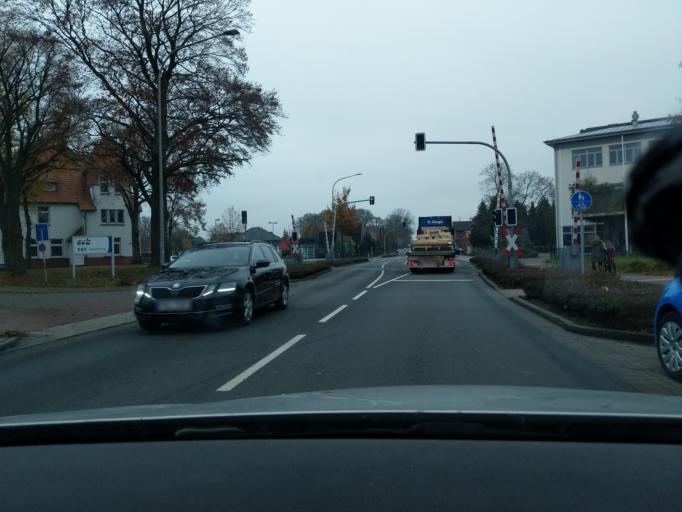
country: DE
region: Lower Saxony
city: Zeven
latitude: 53.2841
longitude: 9.2768
